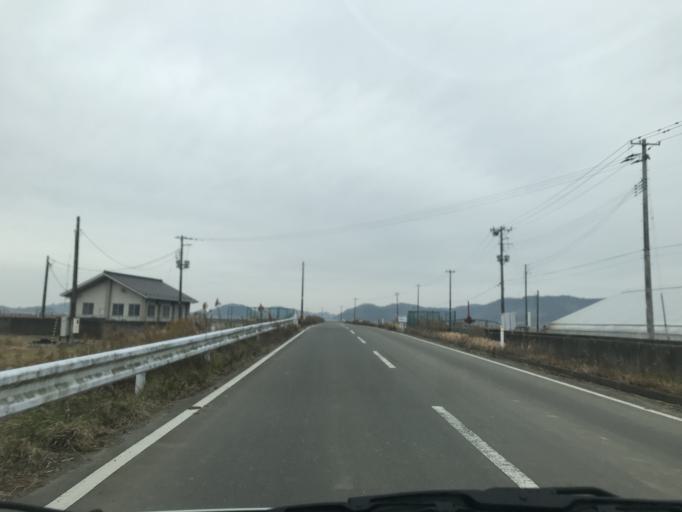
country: JP
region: Iwate
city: Ichinoseki
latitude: 38.7463
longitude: 141.2516
